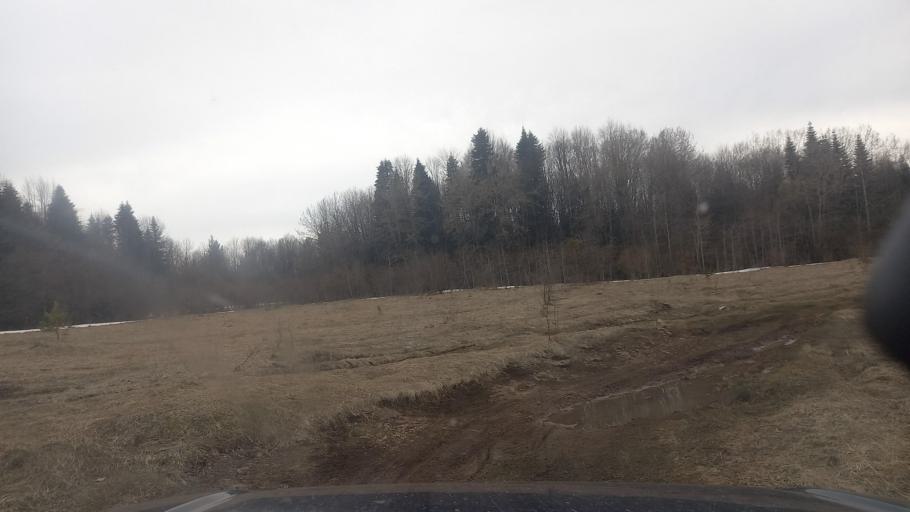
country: RU
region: Adygeya
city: Kamennomostskiy
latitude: 44.1649
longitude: 40.0198
